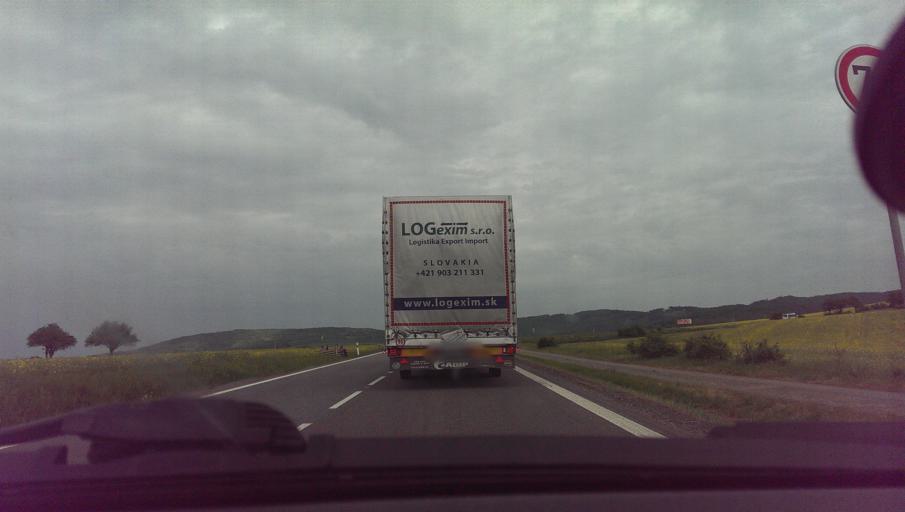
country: CZ
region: Zlin
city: Korycany
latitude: 49.1561
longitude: 17.2068
